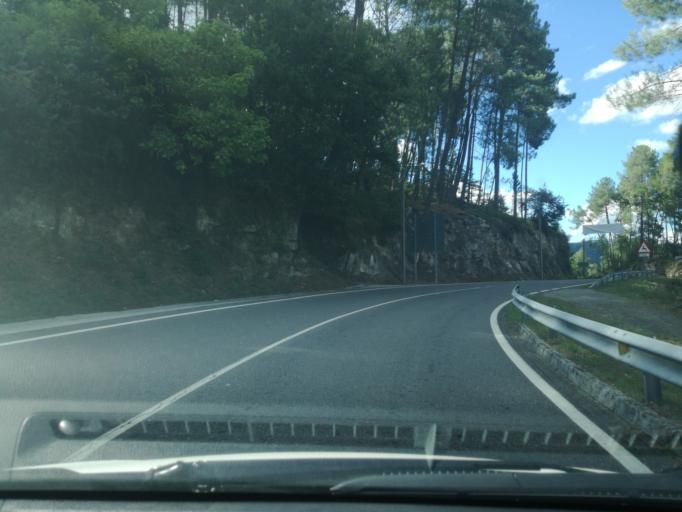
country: ES
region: Galicia
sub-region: Provincia de Ourense
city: Lobios
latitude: 41.9022
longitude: -8.0863
